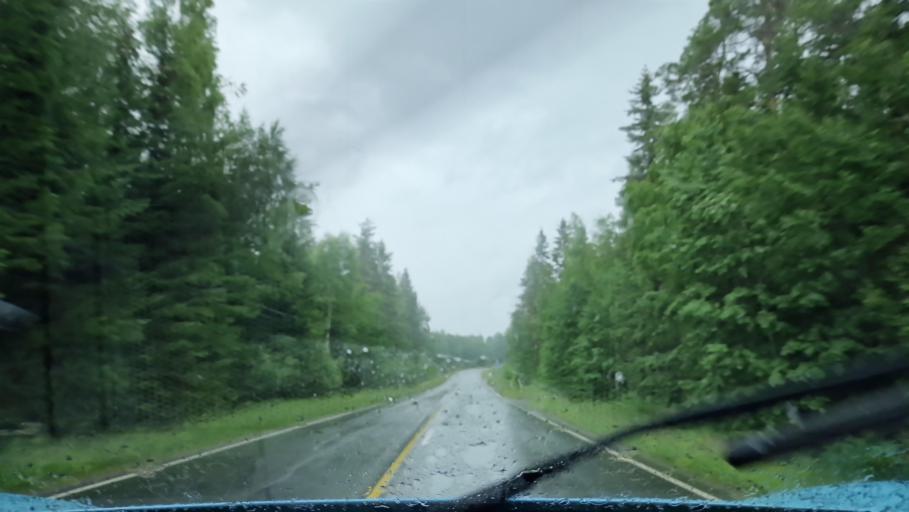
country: FI
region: Southern Ostrobothnia
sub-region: Jaerviseutu
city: Soini
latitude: 62.8247
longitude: 24.3428
